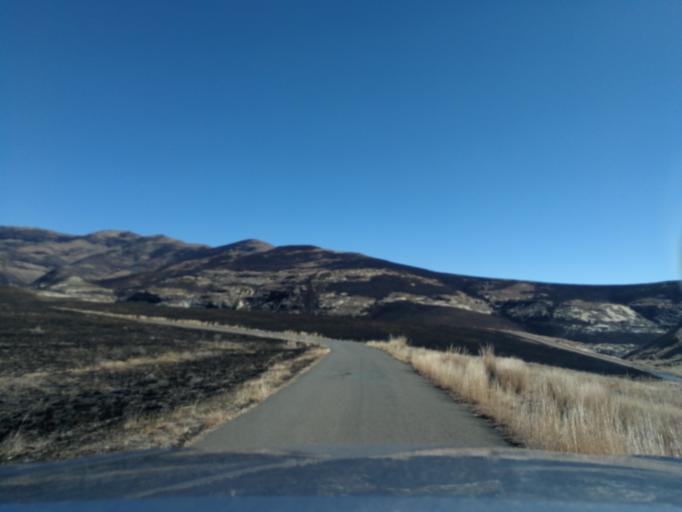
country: ZA
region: Orange Free State
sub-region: Thabo Mofutsanyana District Municipality
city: Phuthaditjhaba
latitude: -28.5128
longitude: 28.6220
